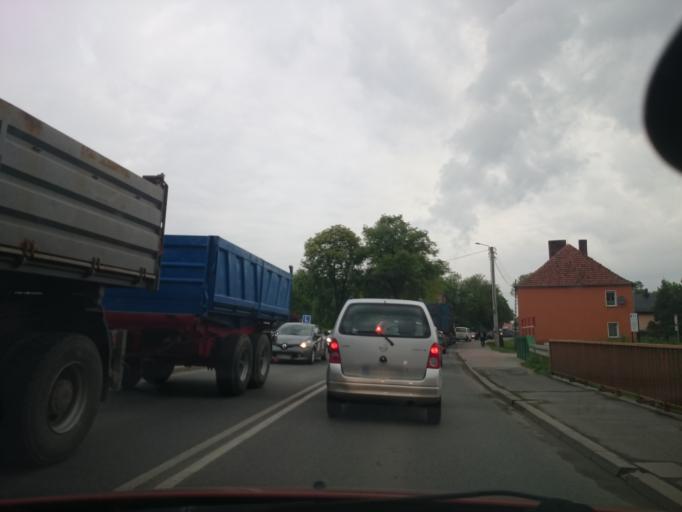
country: PL
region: Opole Voivodeship
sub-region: Powiat opolski
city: Czarnowasy
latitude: 50.7223
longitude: 17.9005
